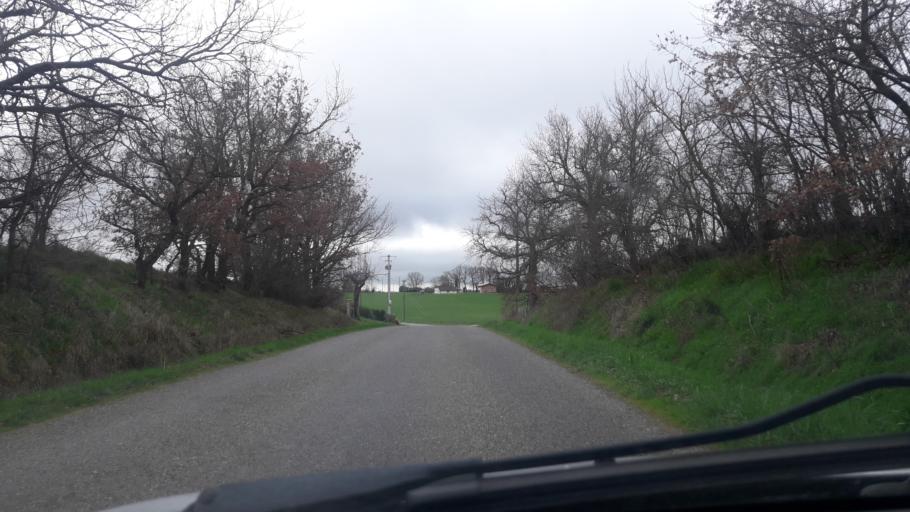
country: FR
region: Midi-Pyrenees
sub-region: Departement du Gers
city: Gimont
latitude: 43.6589
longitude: 1.0122
